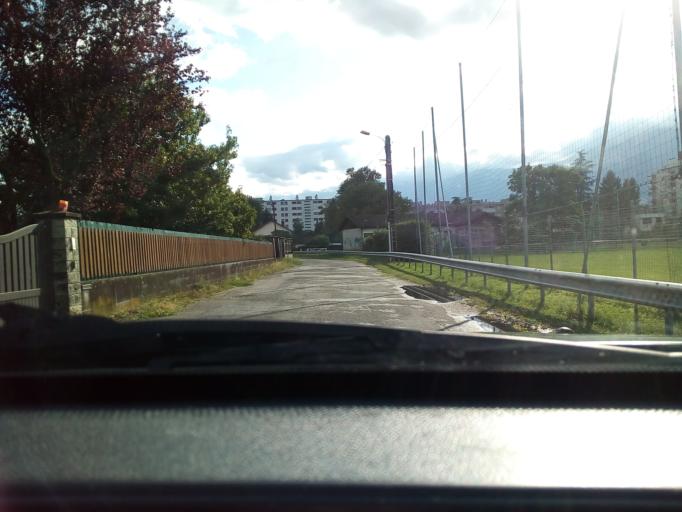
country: FR
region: Rhone-Alpes
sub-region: Departement de l'Isere
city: Saint-Martin-d'Heres
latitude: 45.1662
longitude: 5.7563
